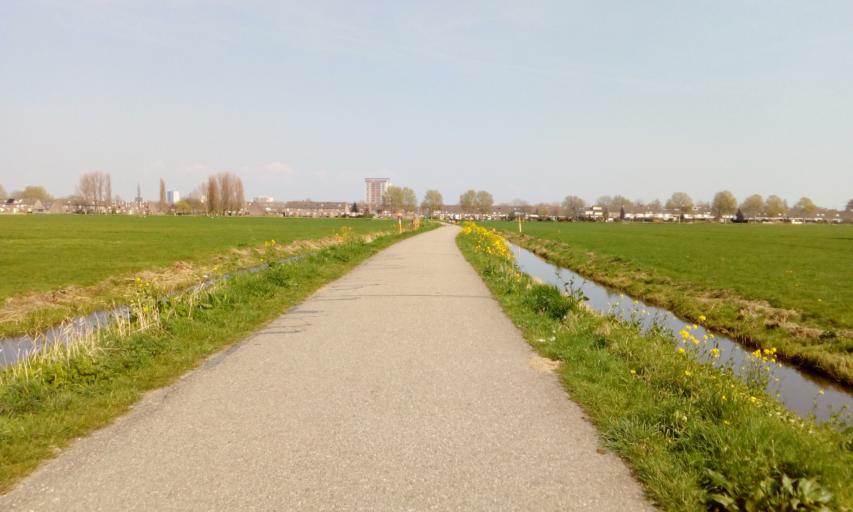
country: NL
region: South Holland
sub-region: Gemeente Spijkenisse
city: Spijkenisse
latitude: 51.8283
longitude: 4.3046
